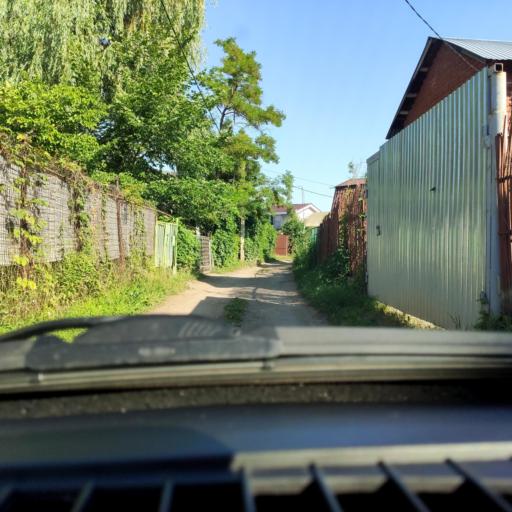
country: RU
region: Samara
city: Zhigulevsk
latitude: 53.4532
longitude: 49.5444
